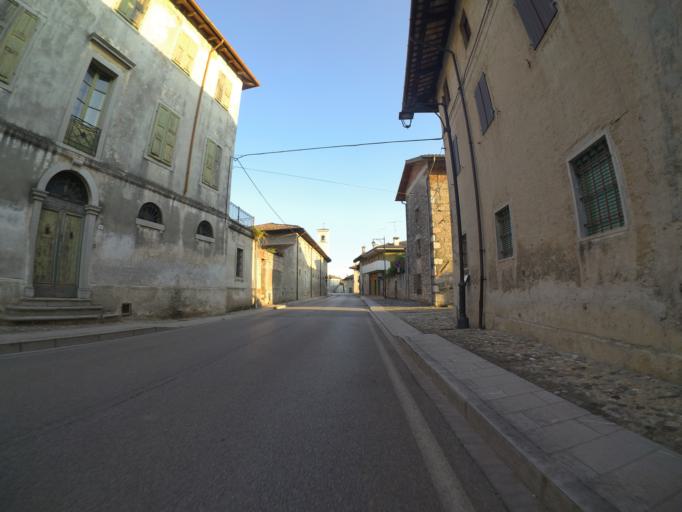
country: IT
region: Friuli Venezia Giulia
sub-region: Provincia di Udine
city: Campoformido
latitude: 46.0079
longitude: 13.1432
